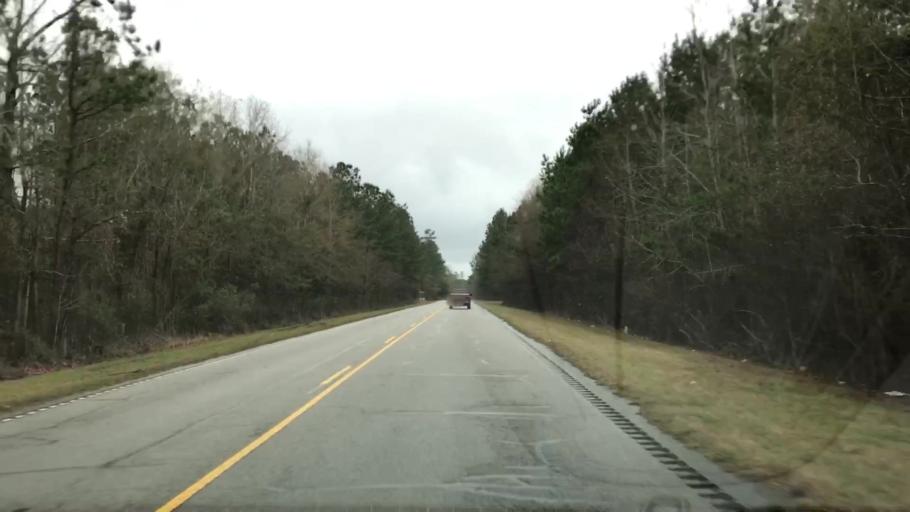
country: US
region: South Carolina
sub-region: Williamsburg County
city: Andrews
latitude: 33.5269
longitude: -79.4894
